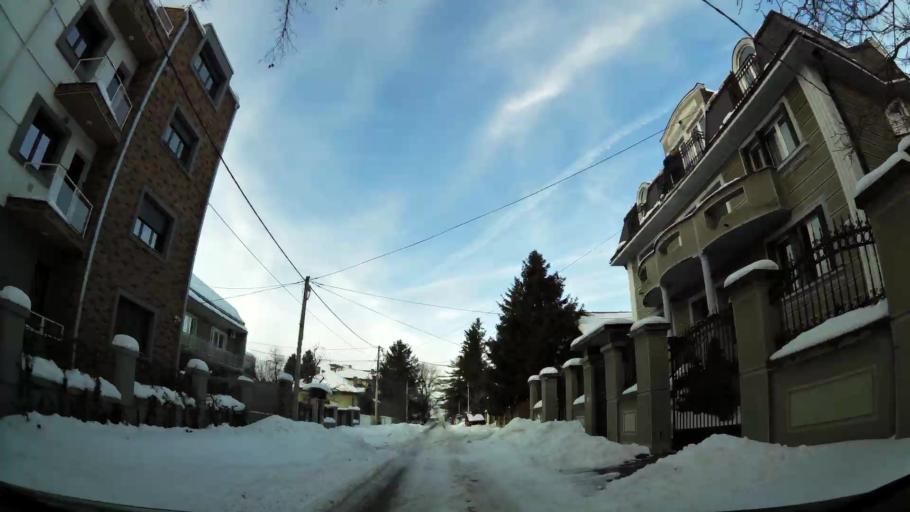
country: RS
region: Central Serbia
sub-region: Belgrade
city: Palilula
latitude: 44.8076
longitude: 20.4992
